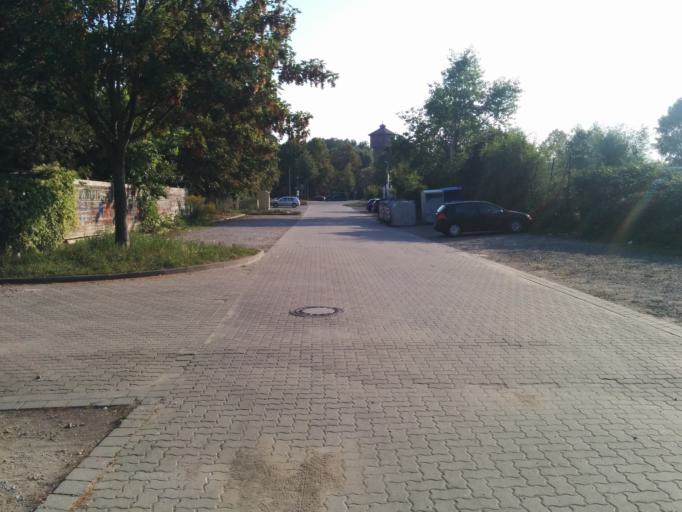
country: DE
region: Lower Saxony
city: Wolfenbuettel
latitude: 52.1562
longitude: 10.5383
